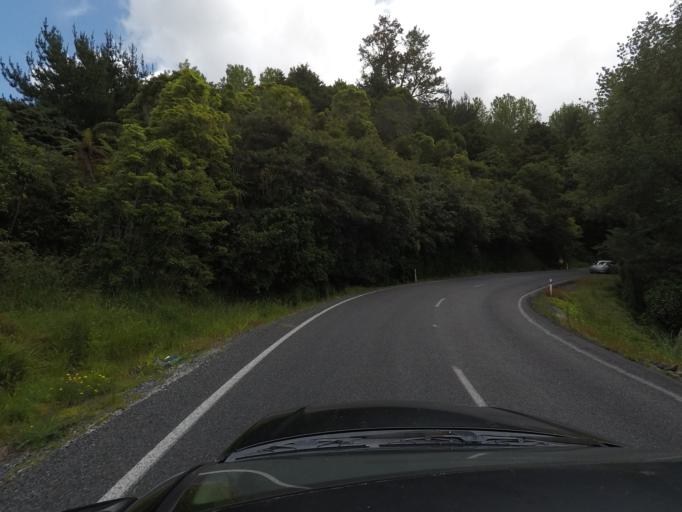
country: NZ
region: Auckland
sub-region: Auckland
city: Warkworth
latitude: -36.5055
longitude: 174.6443
